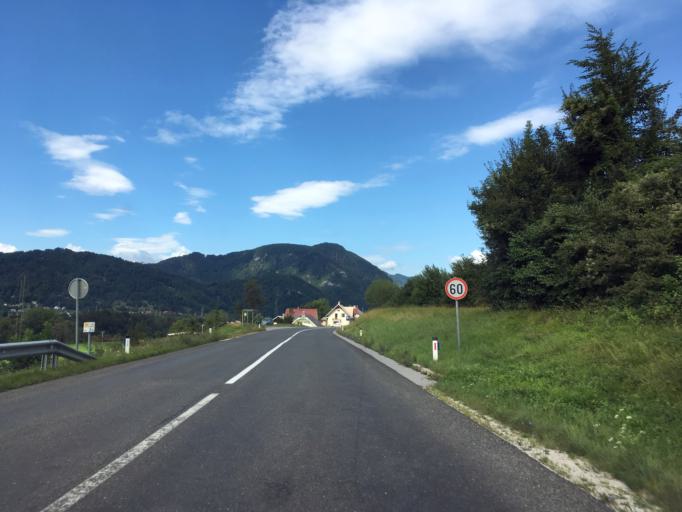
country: SI
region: Zirovnica
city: Zirovnica
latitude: 46.4149
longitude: 14.1217
